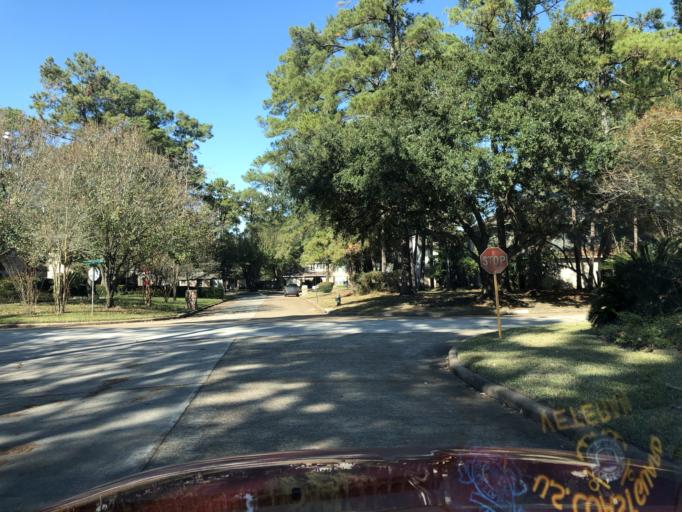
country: US
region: Texas
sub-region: Harris County
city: Tomball
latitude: 30.0263
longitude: -95.5514
